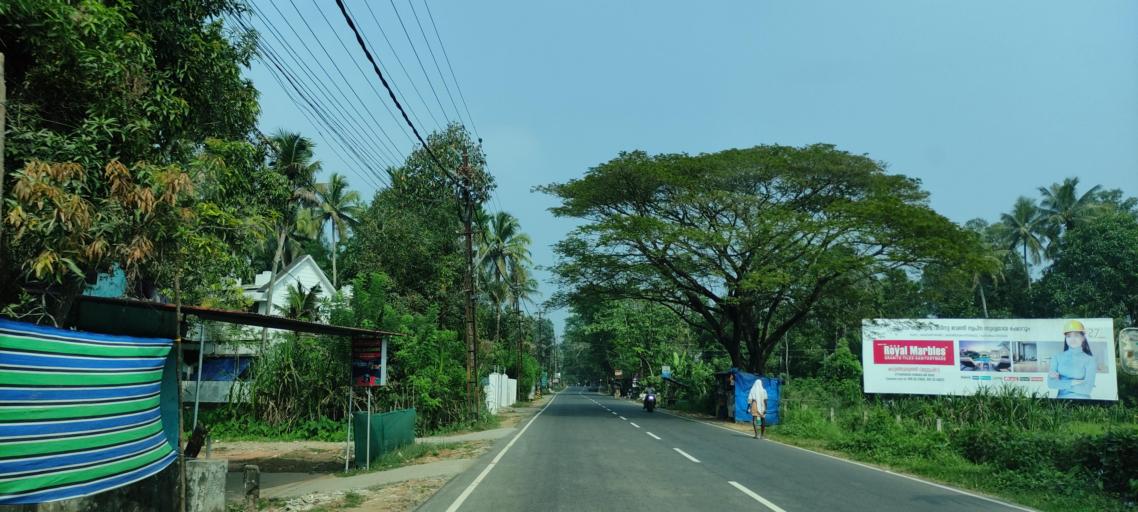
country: IN
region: Kerala
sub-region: Kottayam
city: Vaikam
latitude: 9.7598
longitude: 76.4087
